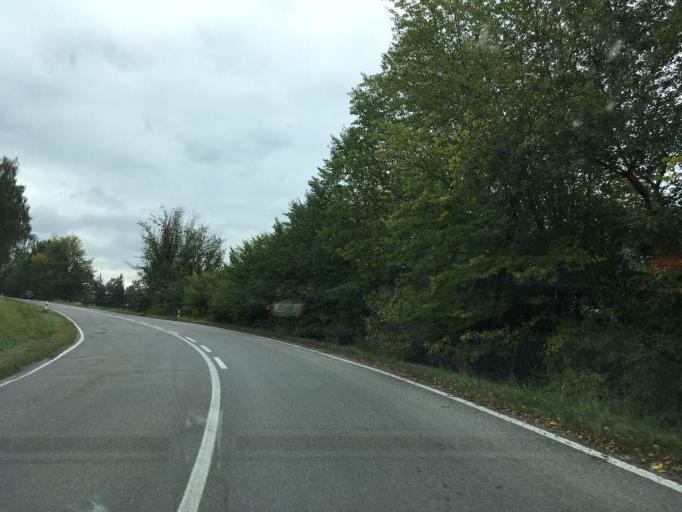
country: CZ
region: Vysocina
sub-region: Okres Pelhrimov
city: Zeliv
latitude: 49.5267
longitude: 15.1696
